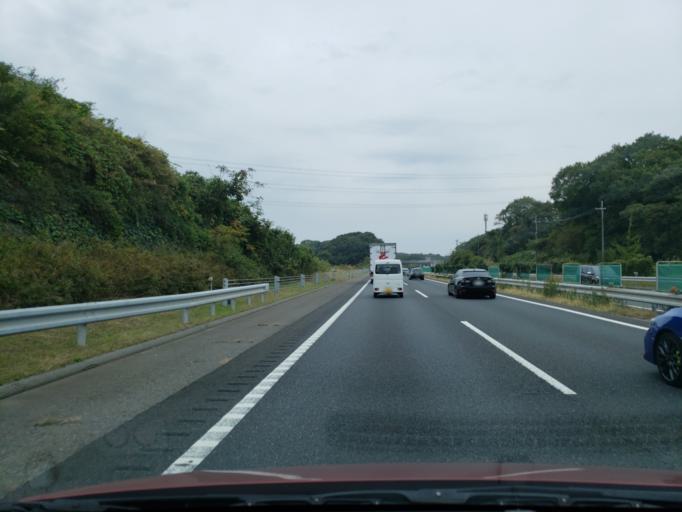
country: JP
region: Hyogo
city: Sandacho
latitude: 34.8321
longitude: 135.1865
